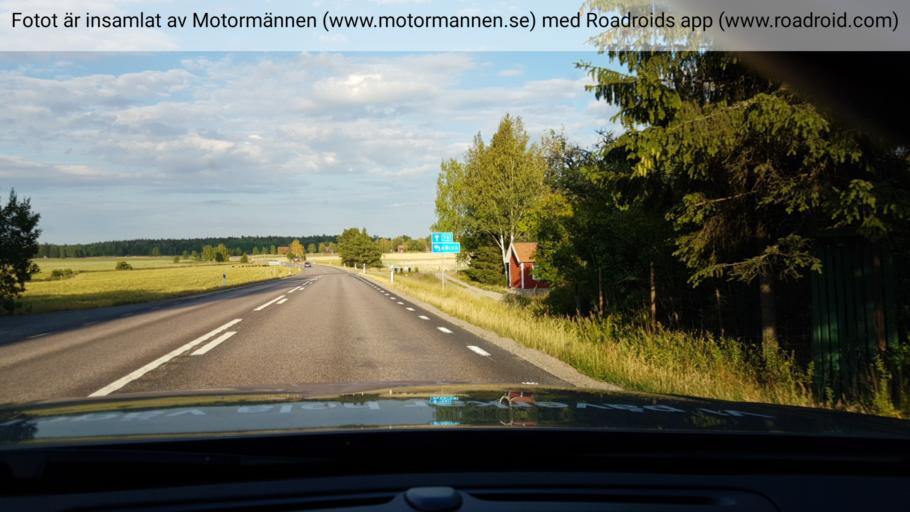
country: SE
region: Uppsala
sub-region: Enkopings Kommun
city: Orsundsbro
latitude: 59.8791
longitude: 17.2639
